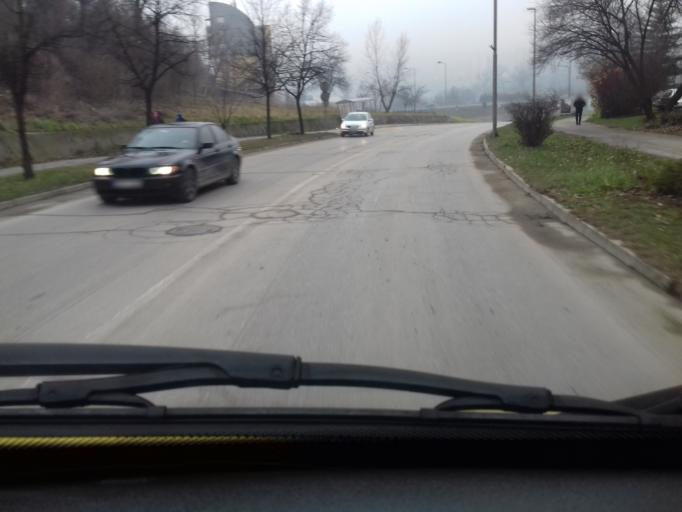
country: BA
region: Federation of Bosnia and Herzegovina
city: Zenica
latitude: 44.1983
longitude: 17.9254
